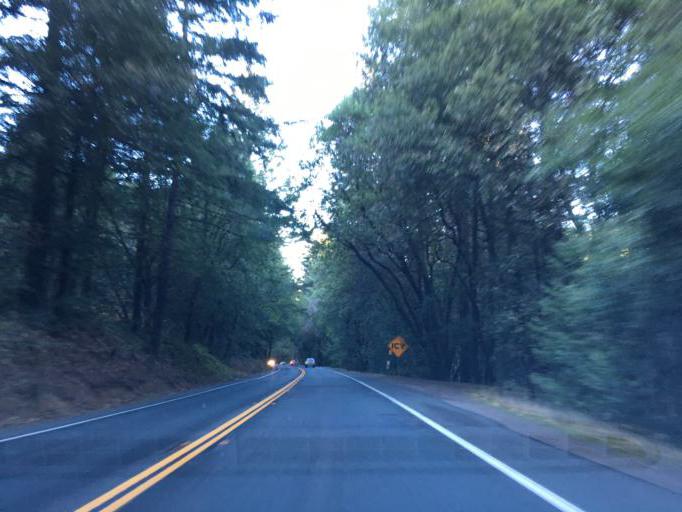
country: US
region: California
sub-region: Mendocino County
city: Brooktrails
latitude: 39.4938
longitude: -123.3648
